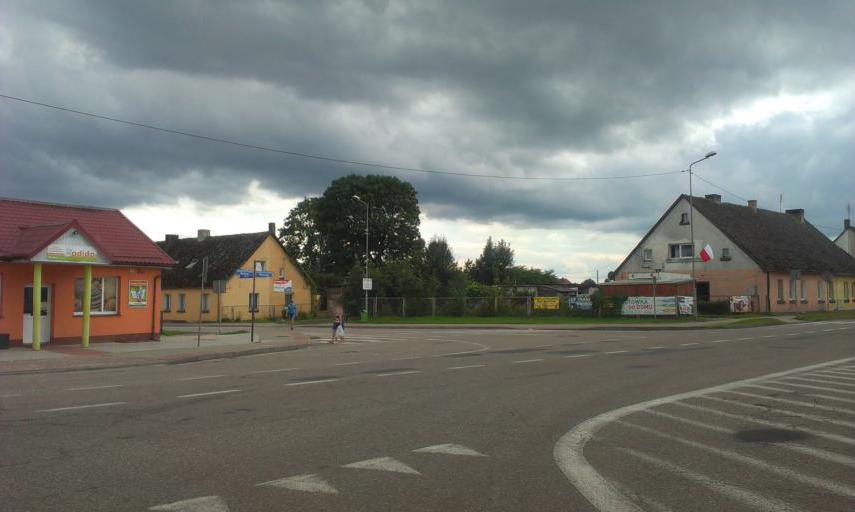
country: PL
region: West Pomeranian Voivodeship
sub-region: Powiat bialogardzki
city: Tychowo
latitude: 53.9271
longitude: 16.2561
